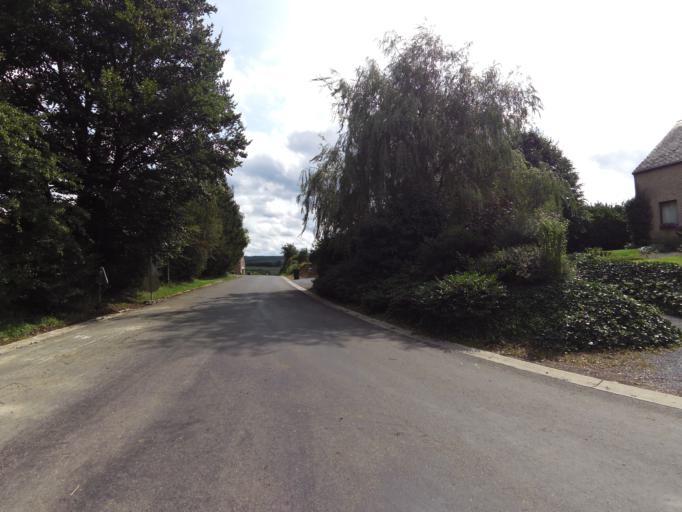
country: BE
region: Wallonia
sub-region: Province de Liege
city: Clavier
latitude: 50.3942
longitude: 5.3983
